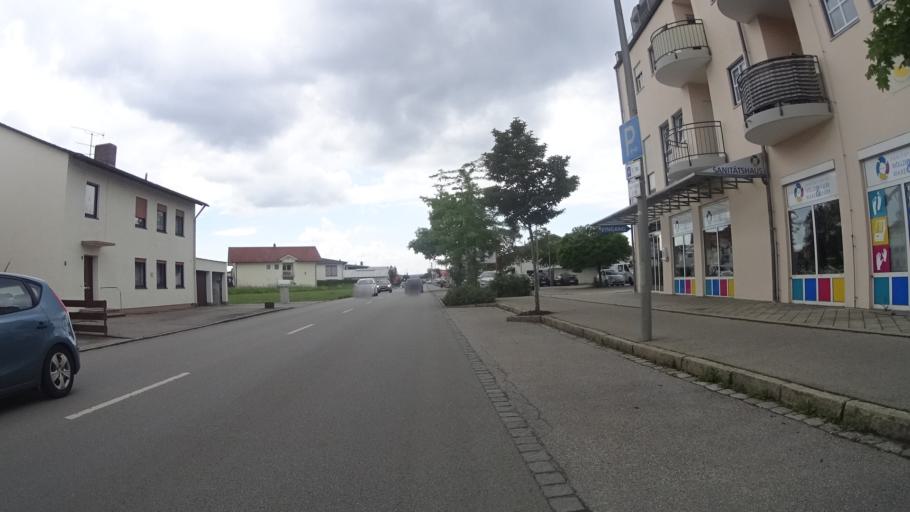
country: DE
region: Bavaria
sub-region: Lower Bavaria
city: Eggenfelden
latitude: 48.3999
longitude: 12.7596
